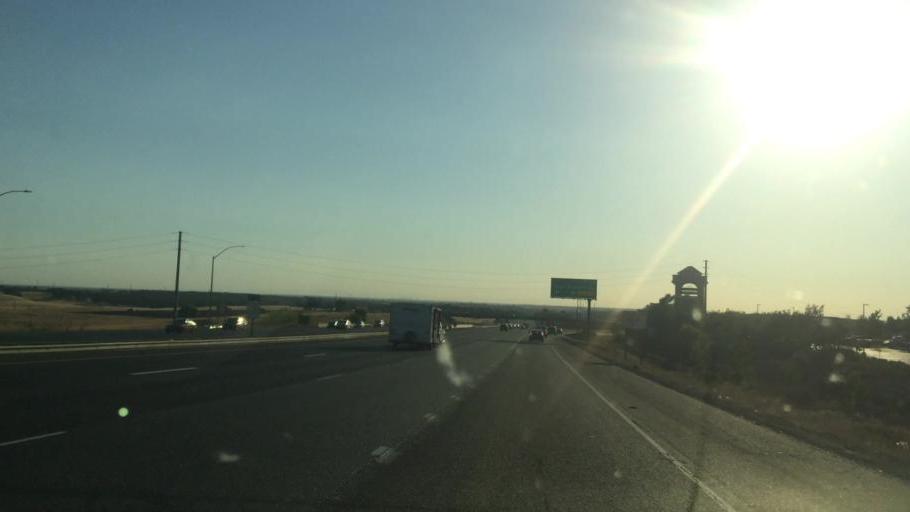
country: US
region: California
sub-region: El Dorado County
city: El Dorado Hills
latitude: 38.6438
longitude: -121.1073
